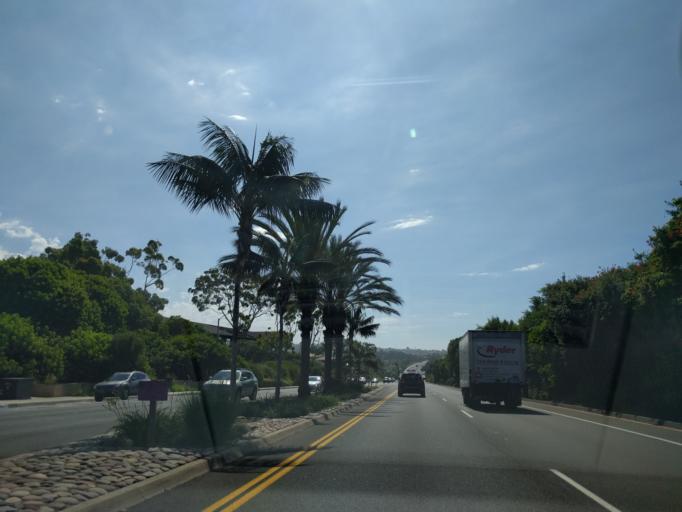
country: US
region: California
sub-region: Orange County
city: Dana Point
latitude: 33.4864
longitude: -117.7268
